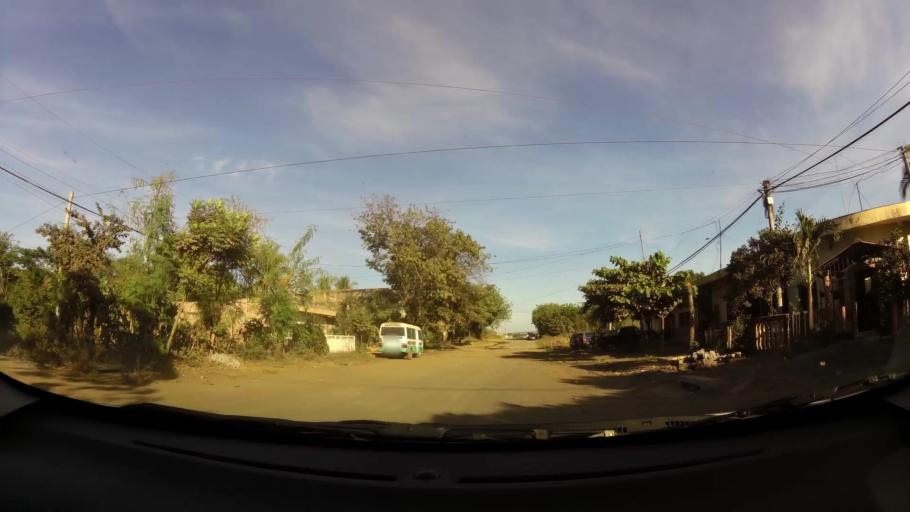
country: SV
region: San Miguel
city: San Miguel
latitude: 13.4581
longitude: -88.1737
